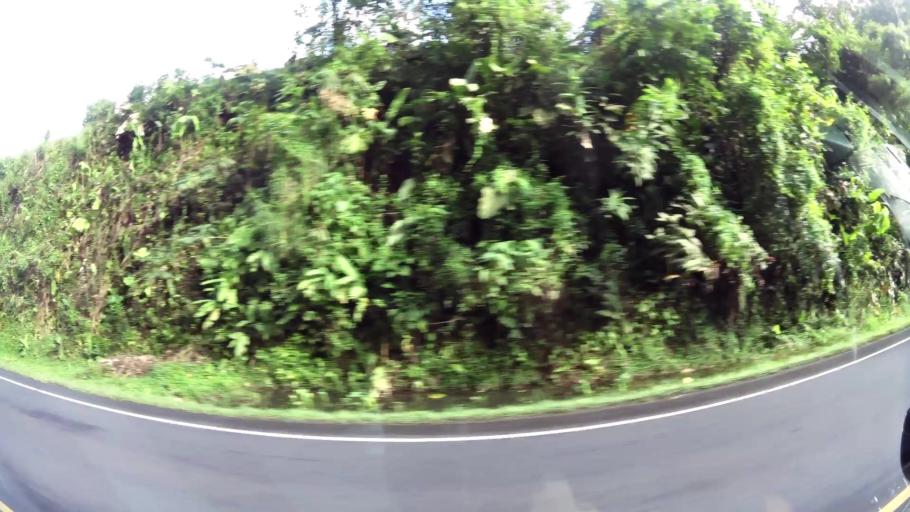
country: CR
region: Limon
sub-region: Canton de Pococi
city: Guapiles
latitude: 10.2033
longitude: -83.8182
